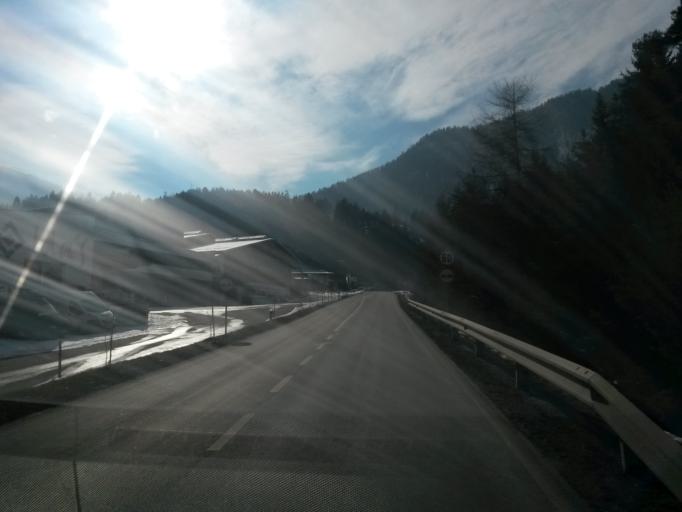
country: AT
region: Tyrol
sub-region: Politischer Bezirk Imst
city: Karrosten
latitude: 47.2160
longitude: 10.7548
